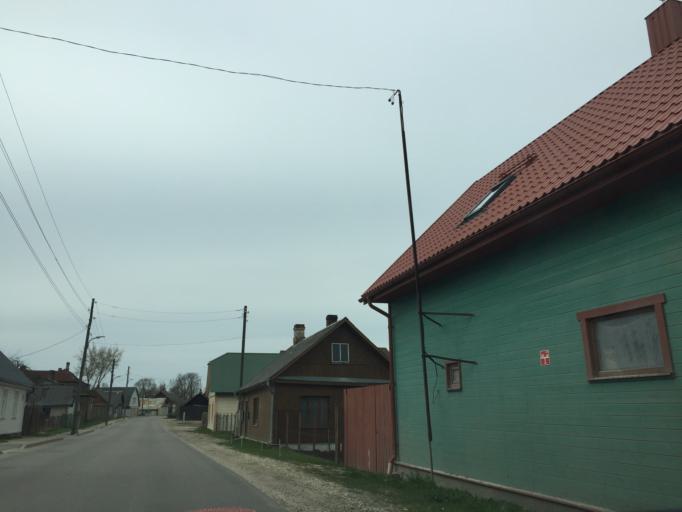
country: LV
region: Ludzas Rajons
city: Ludza
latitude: 56.5535
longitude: 27.7277
